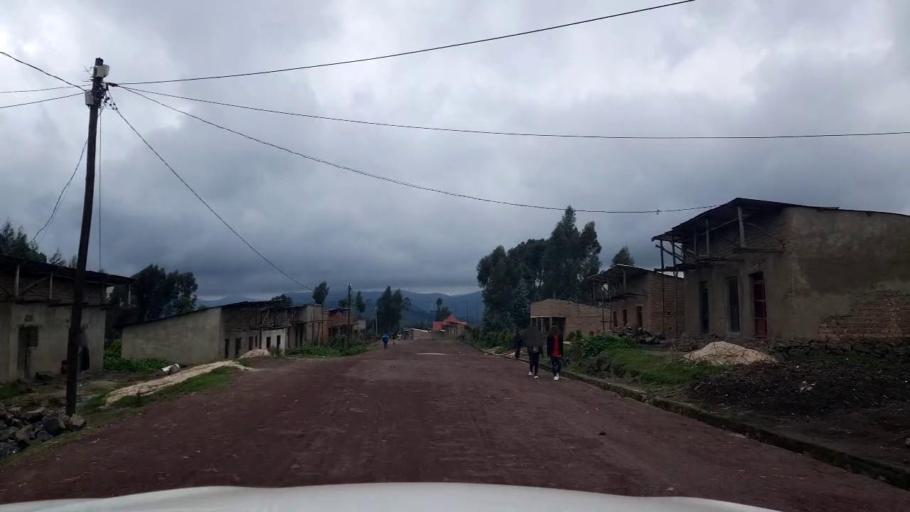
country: RW
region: Northern Province
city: Musanze
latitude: -1.5973
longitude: 29.4522
